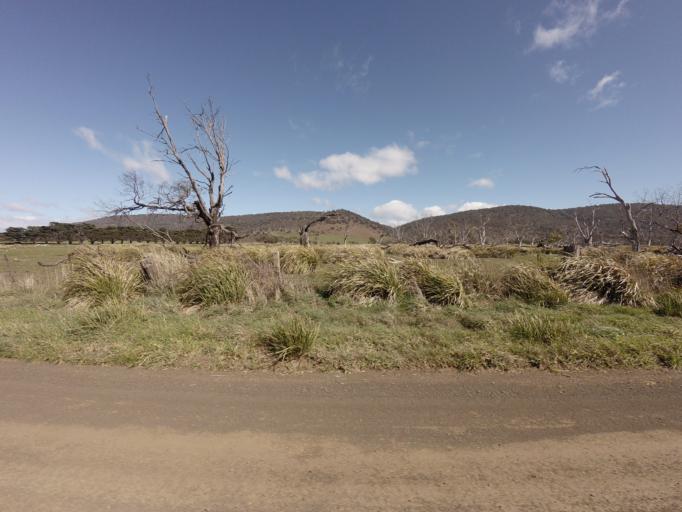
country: AU
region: Tasmania
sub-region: Northern Midlands
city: Evandale
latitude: -41.9484
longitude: 147.4334
